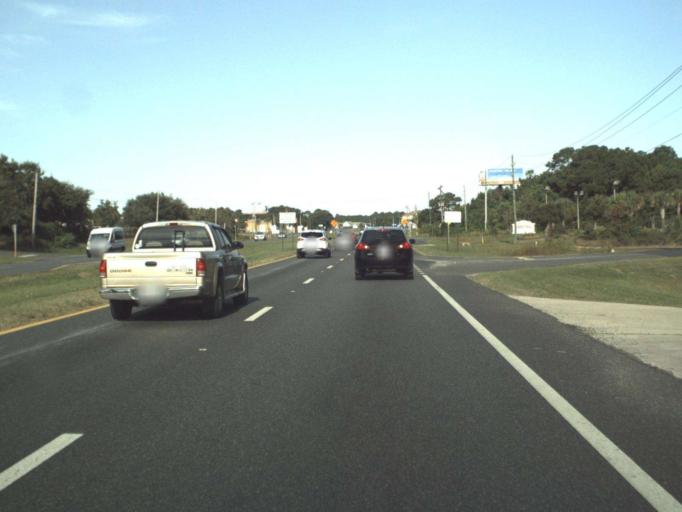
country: US
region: Florida
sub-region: Walton County
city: Miramar Beach
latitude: 30.3805
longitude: -86.3556
